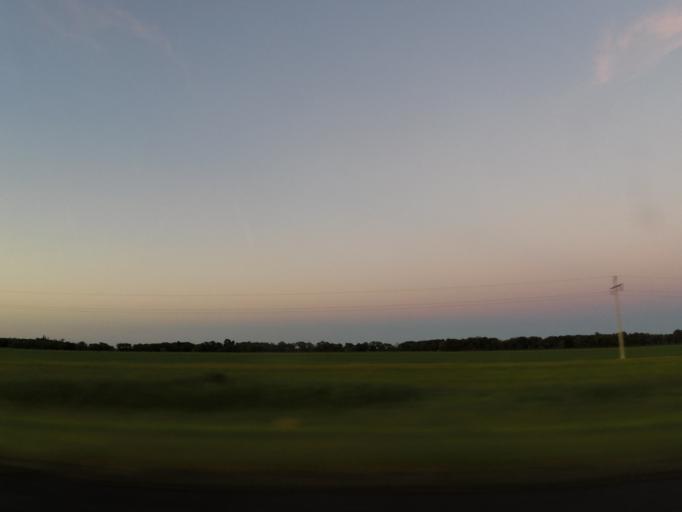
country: US
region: North Dakota
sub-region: Walsh County
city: Grafton
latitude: 48.2475
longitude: -97.1891
